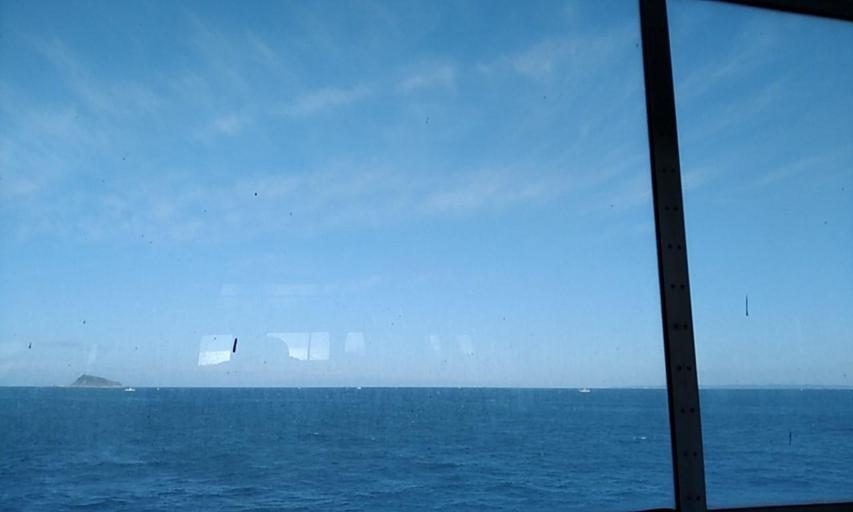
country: JP
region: Mie
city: Toba
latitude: 34.5374
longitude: 136.9535
